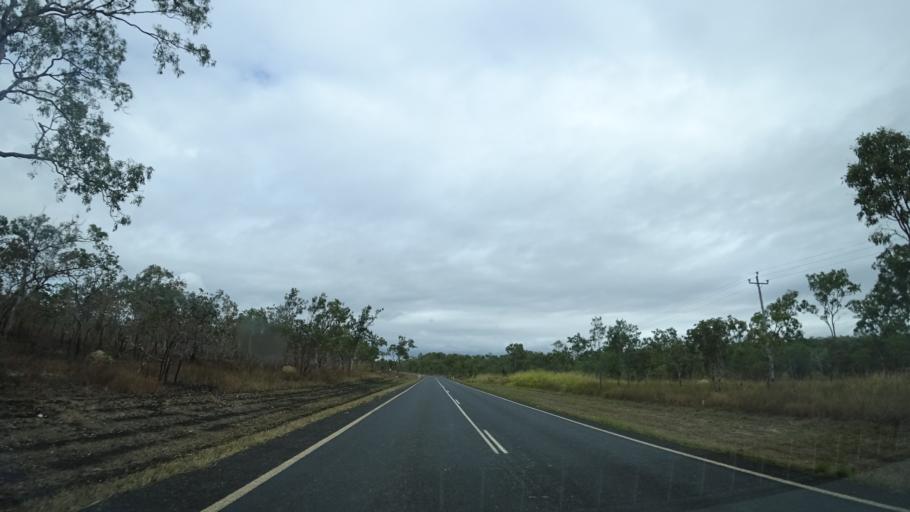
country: AU
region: Queensland
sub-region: Tablelands
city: Mareeba
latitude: -16.7715
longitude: 145.3404
